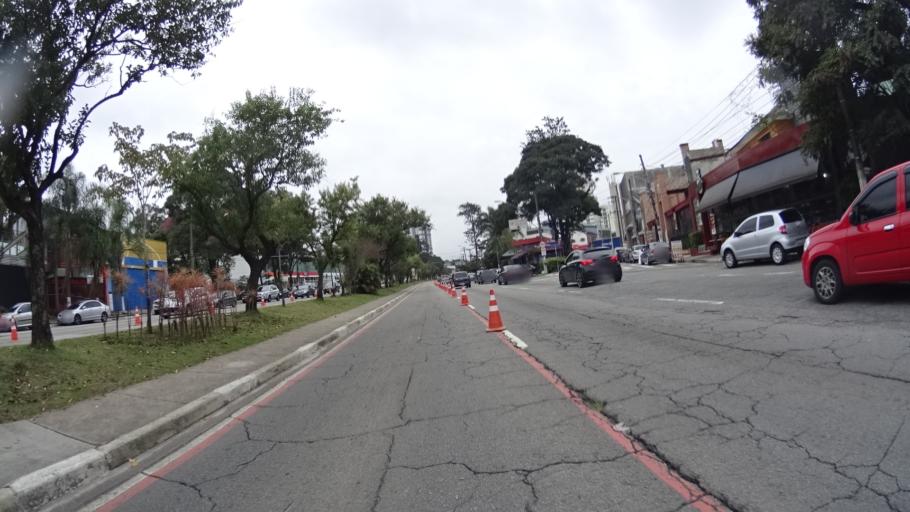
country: BR
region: Sao Paulo
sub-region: Sao Paulo
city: Sao Paulo
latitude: -23.4958
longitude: -46.6119
